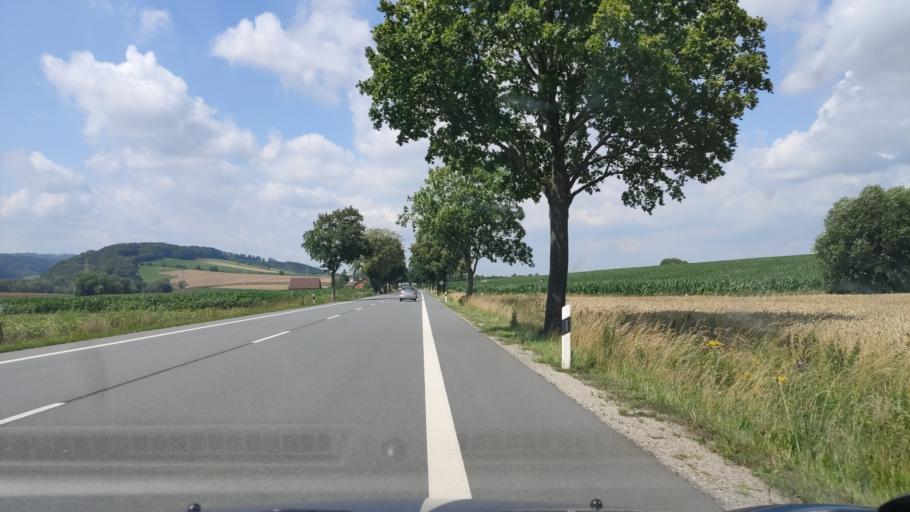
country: DE
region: Lower Saxony
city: Luerdissen
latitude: 51.9510
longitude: 9.6184
